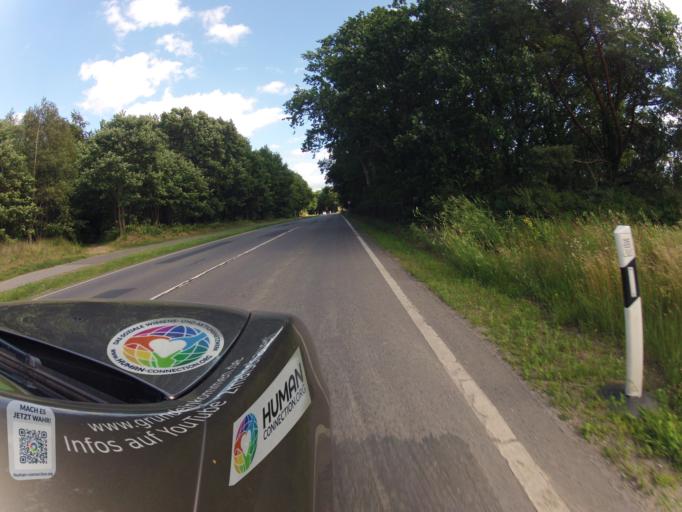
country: DE
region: Mecklenburg-Vorpommern
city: Koserow
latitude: 54.0409
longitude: 14.0107
